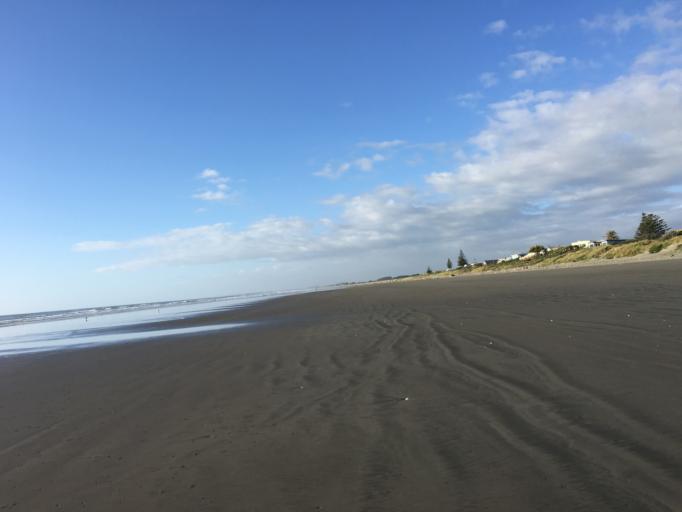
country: NZ
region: Wellington
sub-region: Kapiti Coast District
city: Paraparaumu
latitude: -40.8561
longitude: 175.0288
